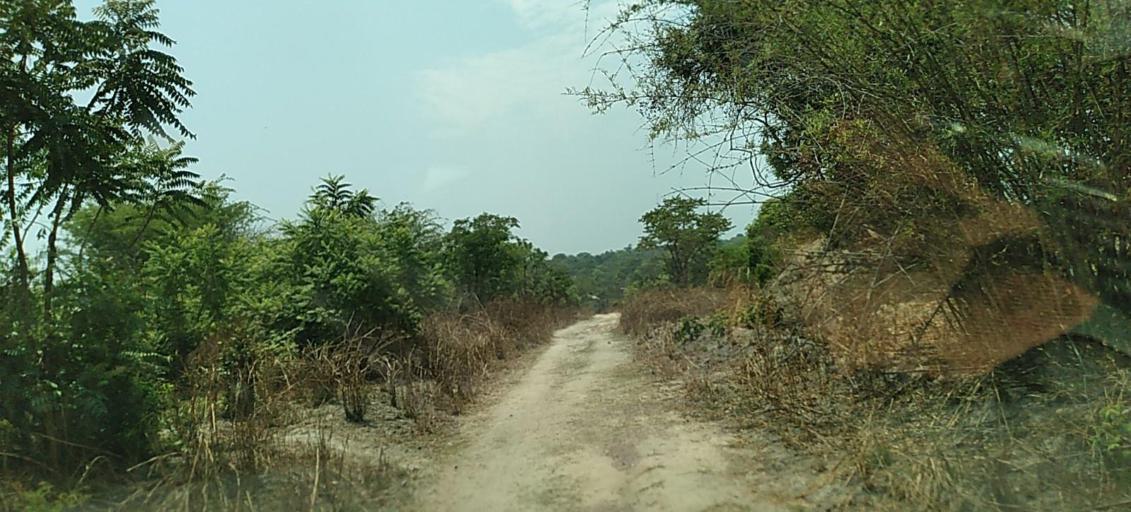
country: ZM
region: Copperbelt
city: Kalulushi
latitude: -12.9458
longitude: 28.1275
